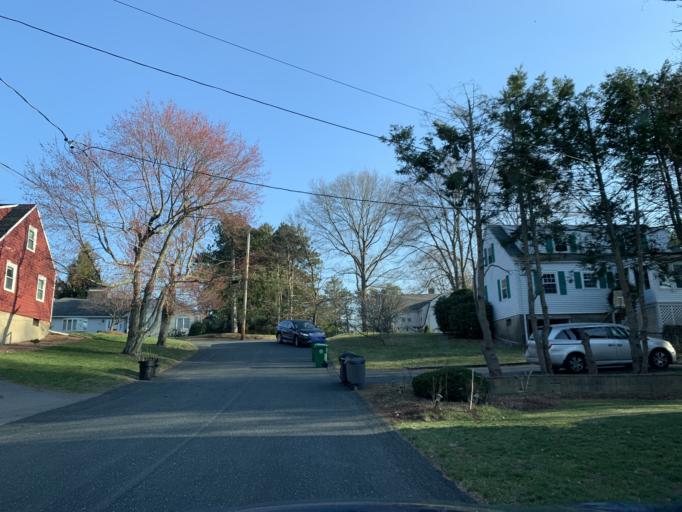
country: US
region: Massachusetts
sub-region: Norfolk County
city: Dedham
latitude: 42.2223
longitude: -71.1775
